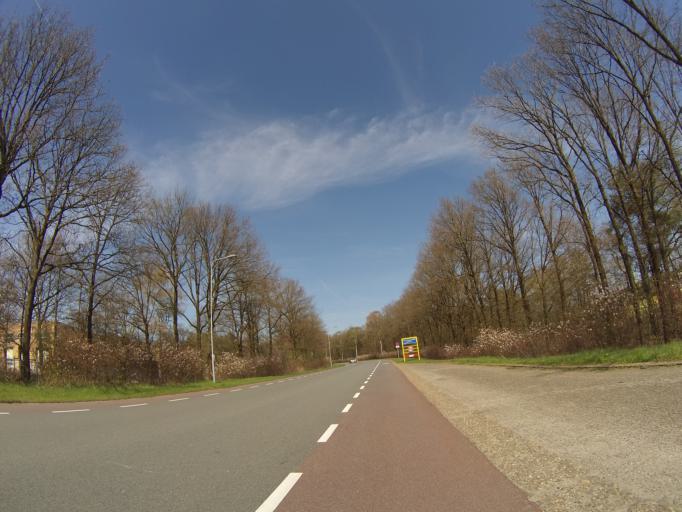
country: NL
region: Utrecht
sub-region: Gemeente Soest
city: Soest
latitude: 52.1214
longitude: 5.3080
